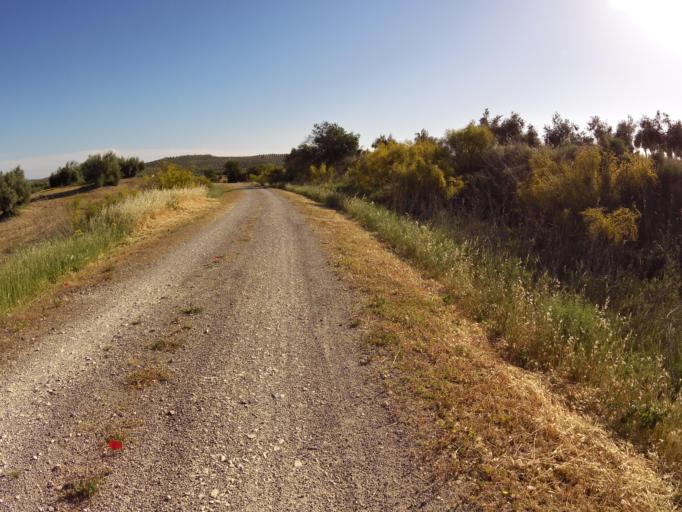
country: ES
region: Andalusia
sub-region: Province of Cordoba
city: Luque
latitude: 37.5774
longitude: -4.2169
